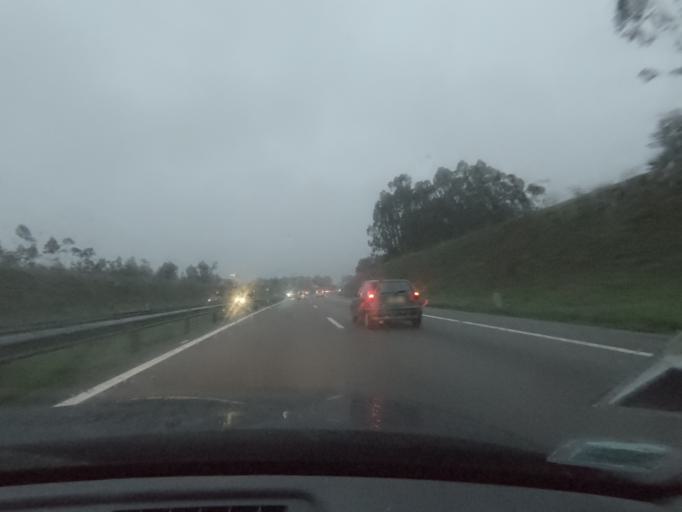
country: PT
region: Porto
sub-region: Matosinhos
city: Santa Cruz do Bispo
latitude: 41.2468
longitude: -8.6951
